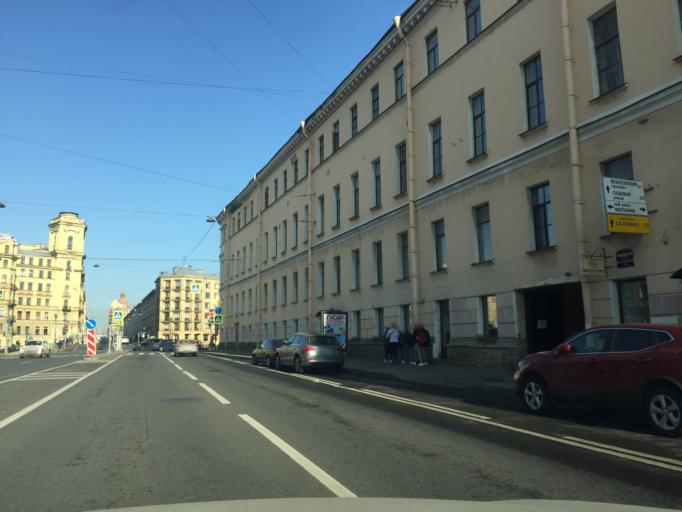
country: RU
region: St.-Petersburg
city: Saint Petersburg
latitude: 59.9182
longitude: 30.3078
